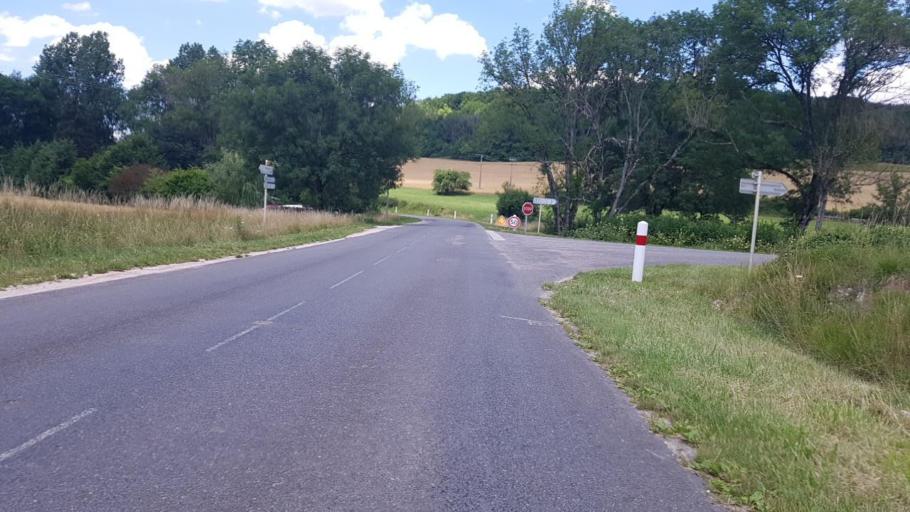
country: FR
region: Lorraine
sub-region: Departement de la Meuse
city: Ligny-en-Barrois
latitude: 48.6464
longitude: 5.4266
